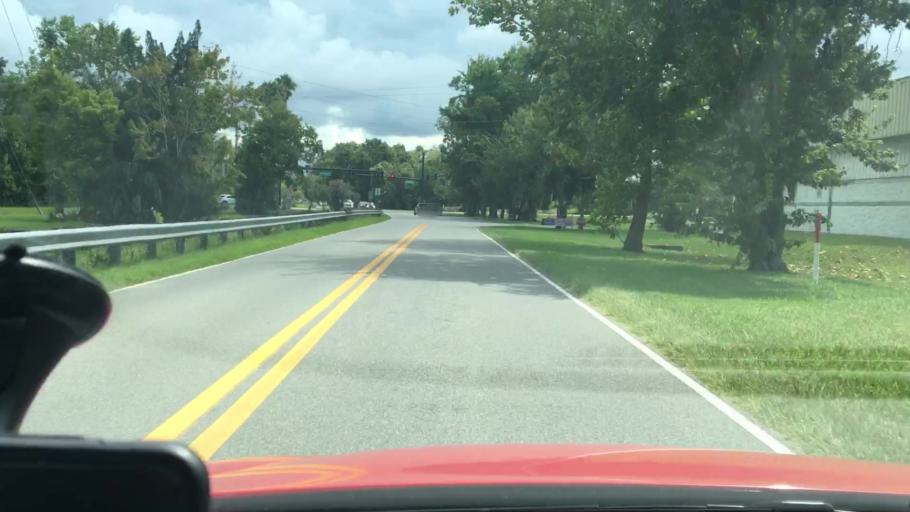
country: US
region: Florida
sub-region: Volusia County
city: Port Orange
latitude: 29.1398
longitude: -80.9979
